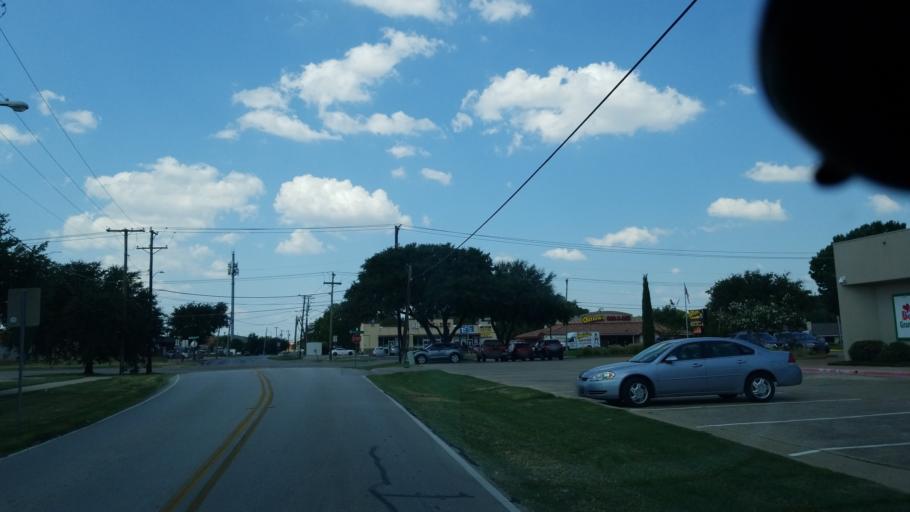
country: US
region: Texas
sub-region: Dallas County
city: Grand Prairie
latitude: 32.7105
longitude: -96.9933
